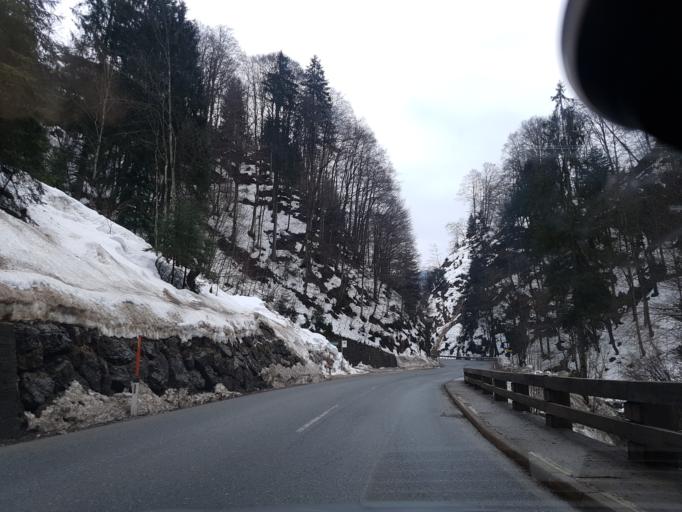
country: AT
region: Tyrol
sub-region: Politischer Bezirk Kufstein
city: Worgl
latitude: 47.4606
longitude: 12.0939
